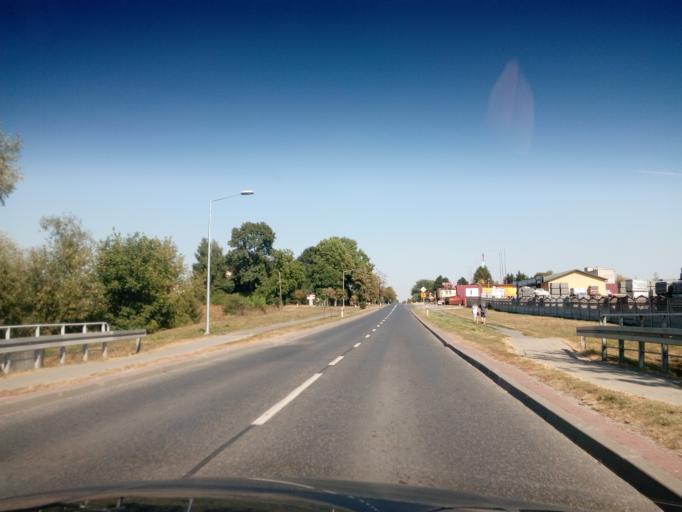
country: PL
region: Lublin Voivodeship
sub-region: Powiat hrubieszowski
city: Hrubieszow
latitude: 50.8065
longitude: 23.9089
